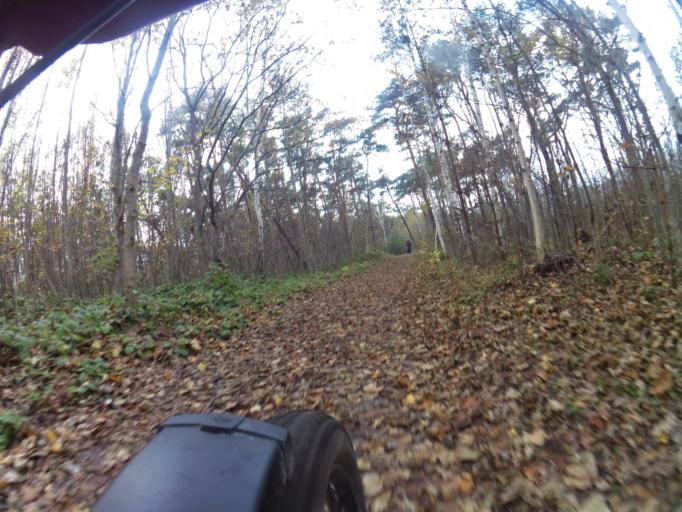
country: PL
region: Pomeranian Voivodeship
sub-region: Powiat pucki
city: Jastarnia
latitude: 54.7281
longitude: 18.6016
